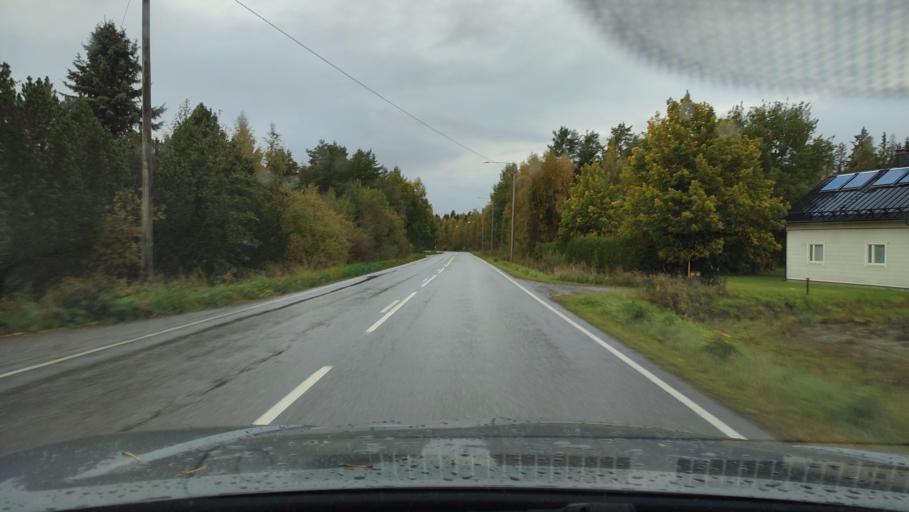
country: FI
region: Southern Ostrobothnia
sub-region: Suupohja
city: Karijoki
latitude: 62.2393
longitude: 21.6041
